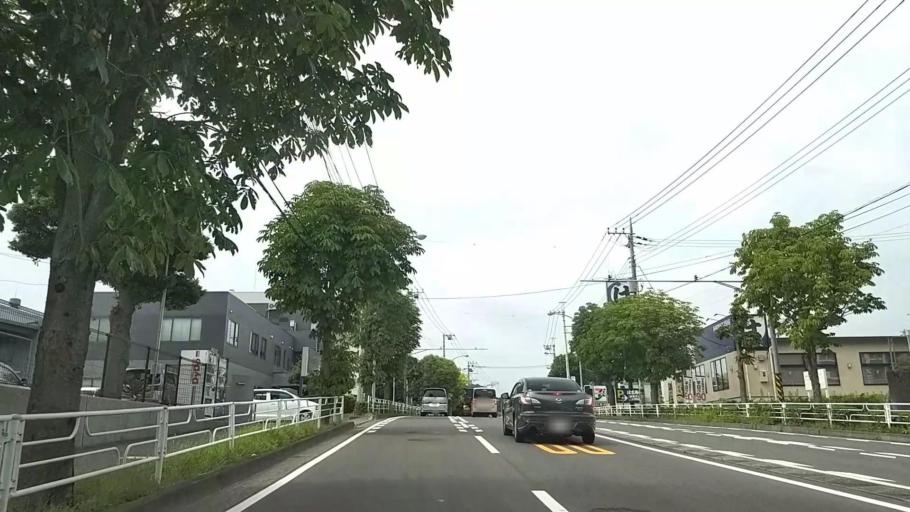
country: JP
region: Kanagawa
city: Minami-rinkan
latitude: 35.4955
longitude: 139.5351
